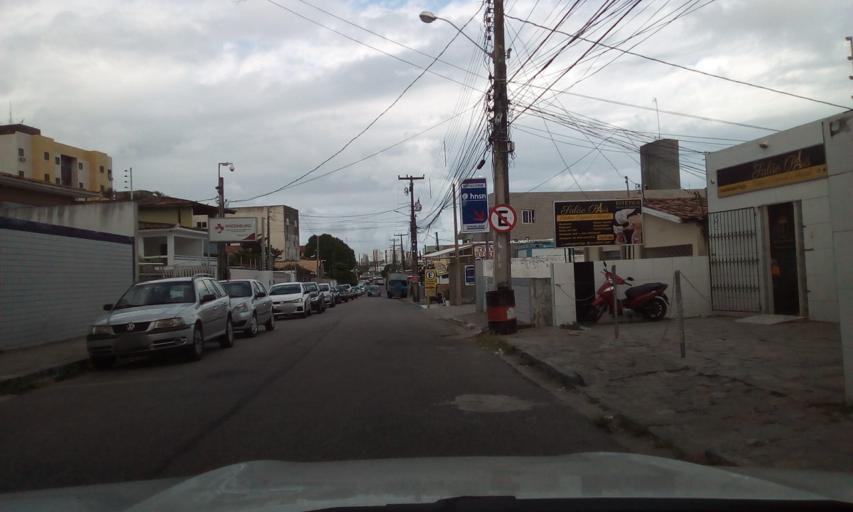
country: BR
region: Paraiba
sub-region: Joao Pessoa
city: Joao Pessoa
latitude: -7.1325
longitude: -34.8588
